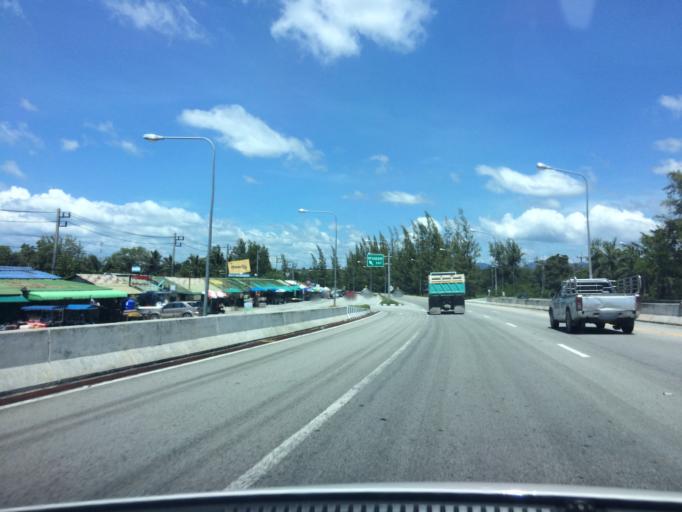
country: TH
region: Phuket
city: Thalang
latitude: 8.2052
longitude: 98.2994
